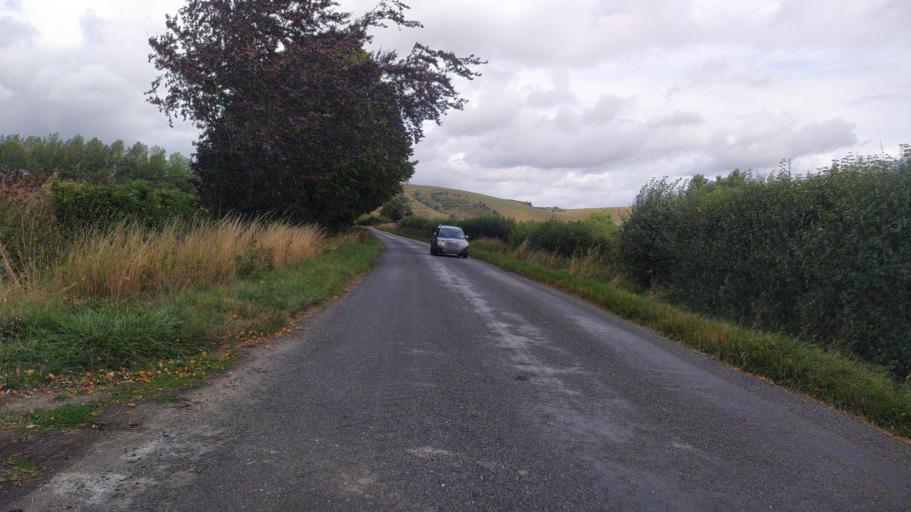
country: GB
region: England
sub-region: Hampshire
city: Cowplain
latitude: 50.9864
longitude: -1.0256
